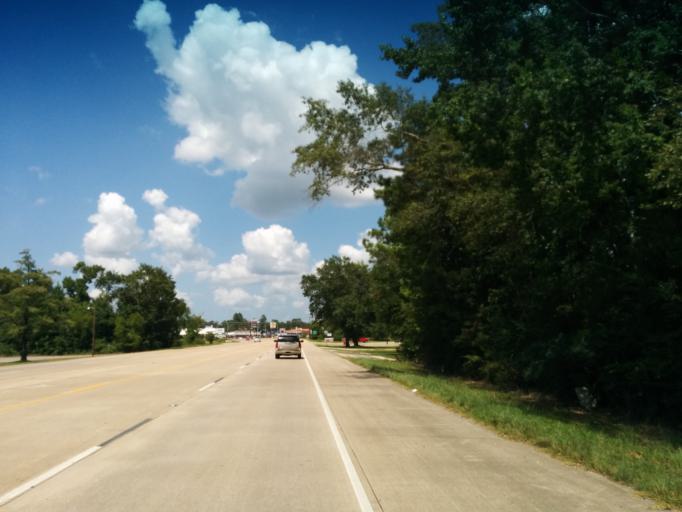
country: US
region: Texas
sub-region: Jasper County
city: Buna
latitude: 30.4386
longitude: -93.9715
